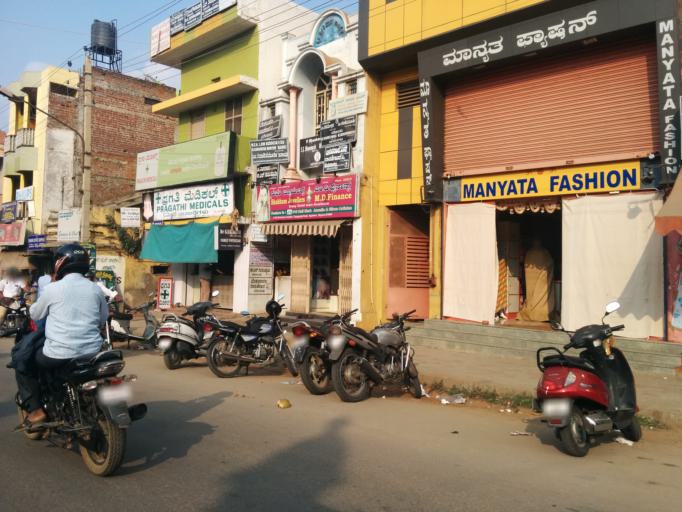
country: IN
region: Karnataka
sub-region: Mysore
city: Mysore
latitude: 12.2971
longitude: 76.6518
